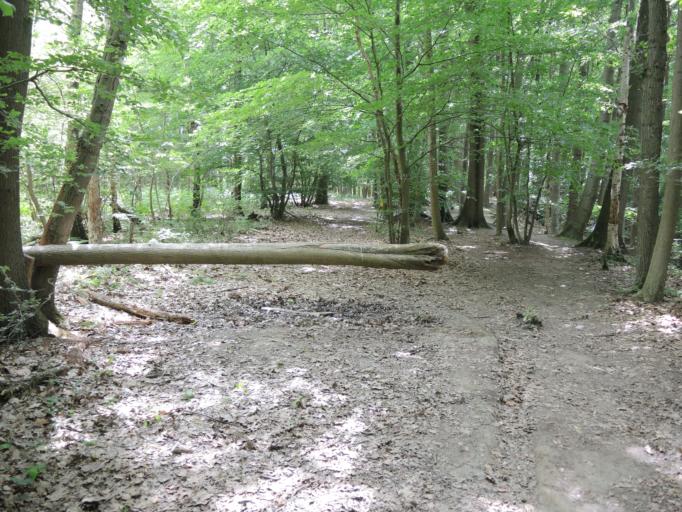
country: BE
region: Flanders
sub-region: Provincie Vlaams-Brabant
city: Asse
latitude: 50.9278
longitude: 4.1540
